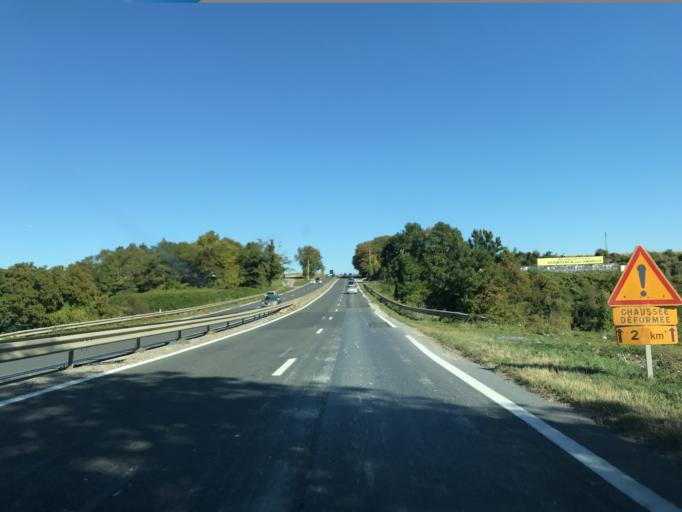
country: FR
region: Ile-de-France
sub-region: Departement de Seine-et-Marne
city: Charny
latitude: 48.9546
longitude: 2.7805
